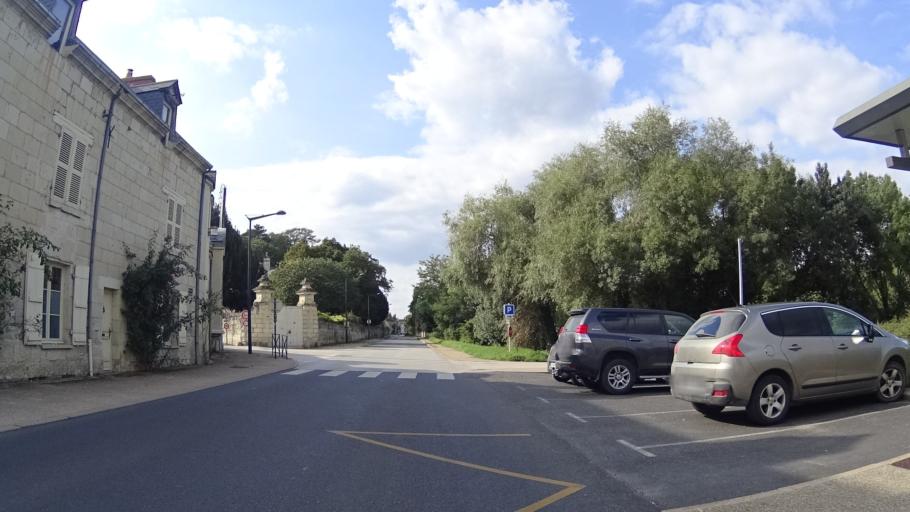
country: FR
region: Pays de la Loire
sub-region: Departement de Maine-et-Loire
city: Villebernier
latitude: 47.2421
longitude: -0.0268
